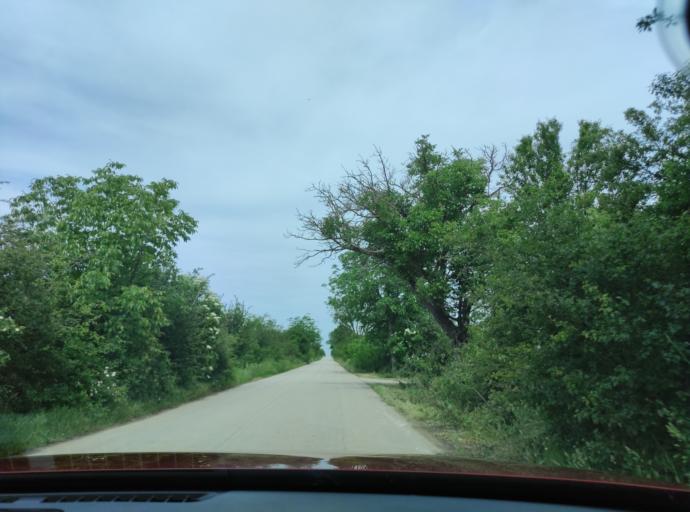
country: BG
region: Pleven
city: Iskur
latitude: 43.5239
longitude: 24.3205
